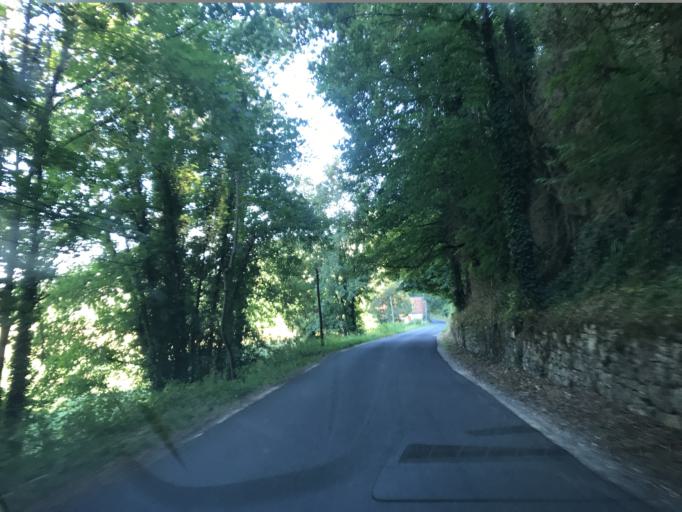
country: FR
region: Aquitaine
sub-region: Departement de la Dordogne
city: Carsac-Aillac
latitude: 44.8224
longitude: 1.2404
